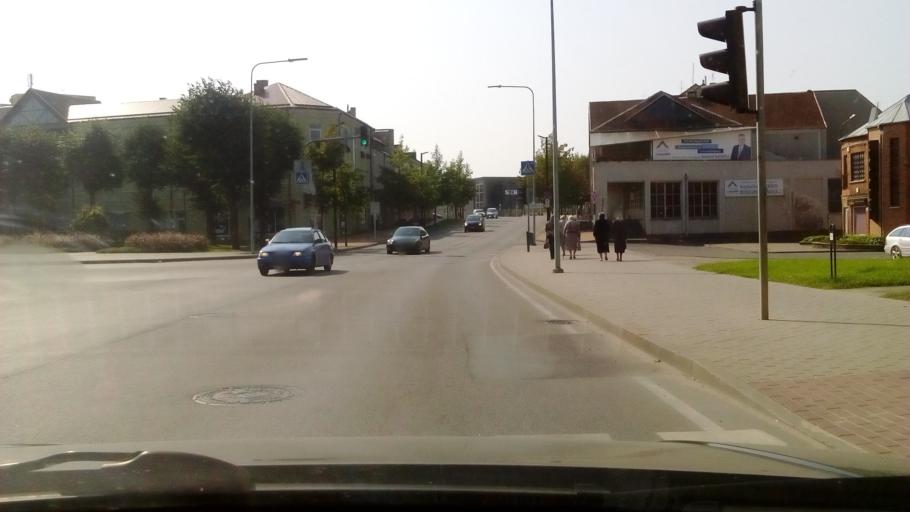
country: LT
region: Alytaus apskritis
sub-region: Alytus
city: Alytus
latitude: 54.3993
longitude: 24.0483
